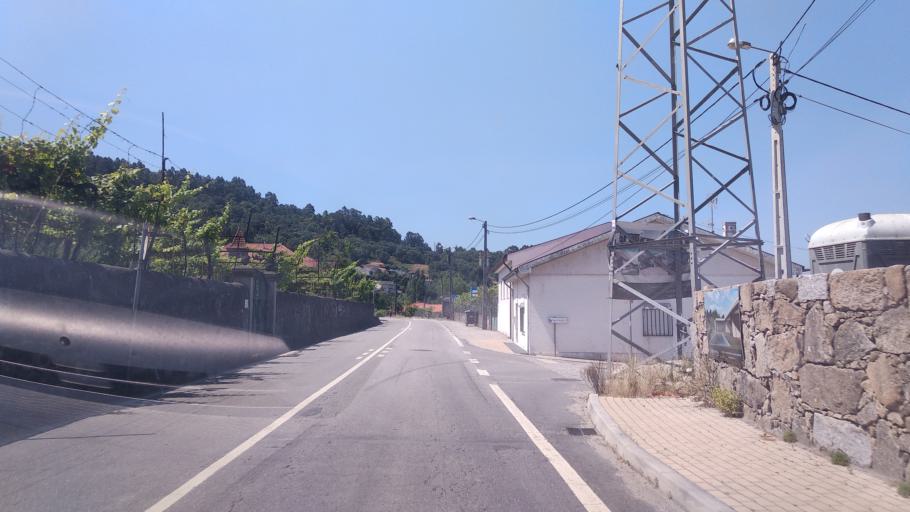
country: PT
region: Braga
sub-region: Braga
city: Adaufe
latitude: 41.5802
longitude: -8.4080
